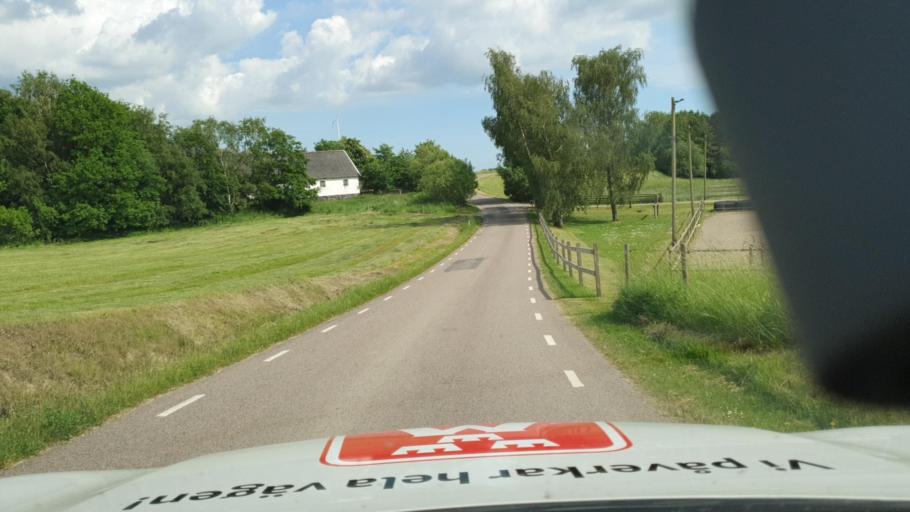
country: SE
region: Skane
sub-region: Skurups Kommun
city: Skurup
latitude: 55.5187
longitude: 13.4772
